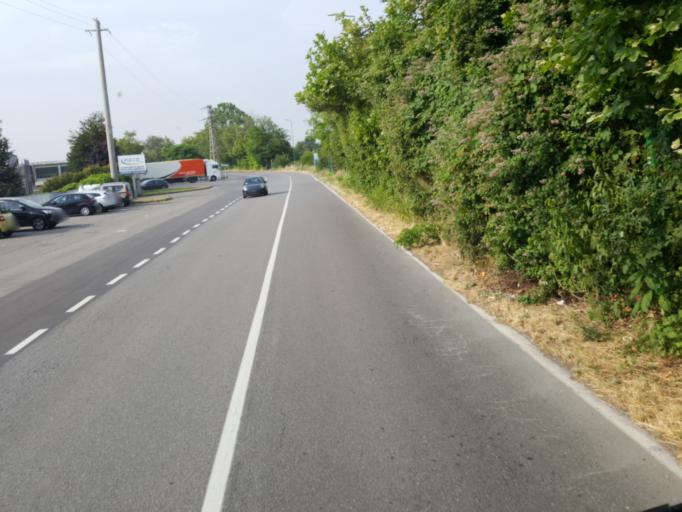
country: IT
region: Lombardy
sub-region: Provincia di Bergamo
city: Grassobbio
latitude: 45.6558
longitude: 9.7072
